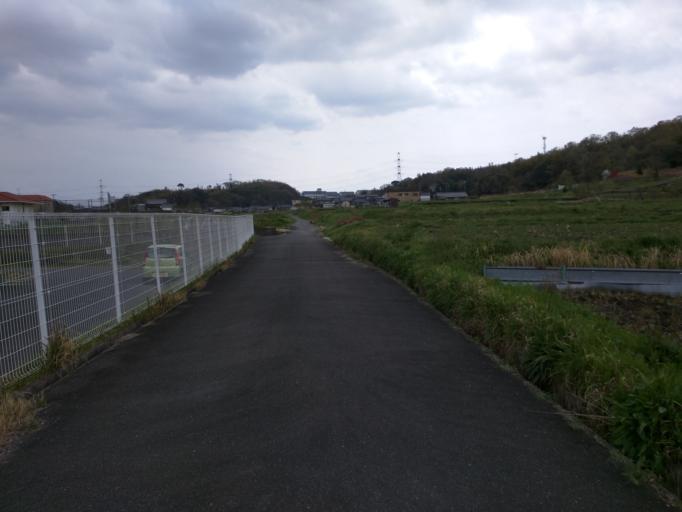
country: JP
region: Kyoto
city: Tanabe
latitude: 34.7625
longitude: 135.7828
